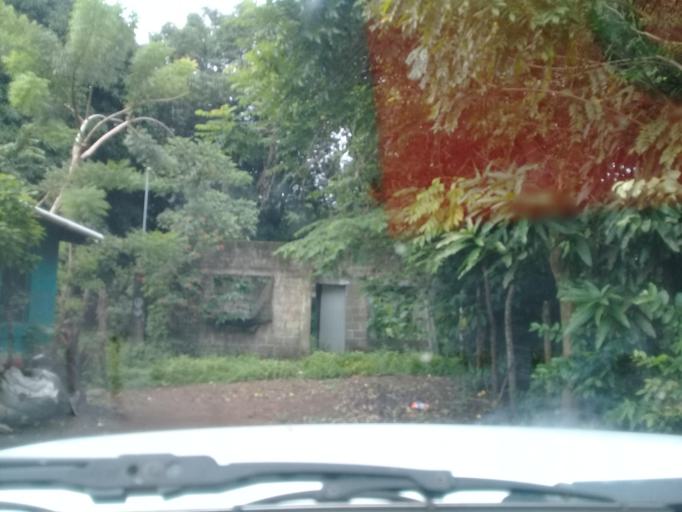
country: MX
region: Veracruz
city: Comoapan
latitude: 18.4096
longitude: -95.1579
